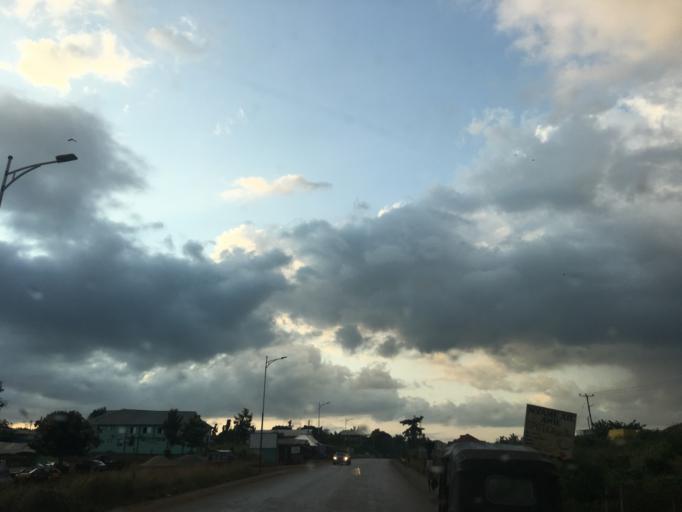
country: GH
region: Western
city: Bibiani
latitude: 6.7821
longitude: -2.5156
